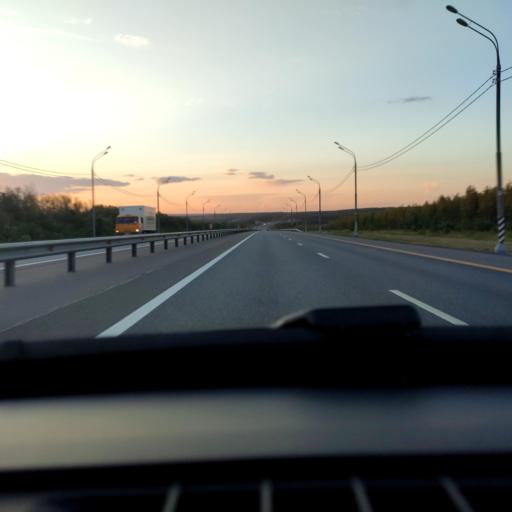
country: RU
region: Lipetsk
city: Khlevnoye
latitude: 52.2729
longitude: 39.0566
